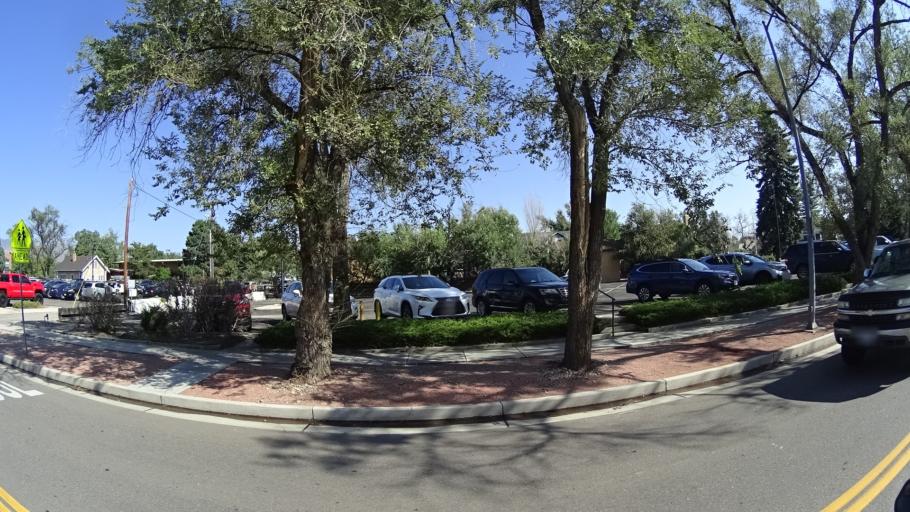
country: US
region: Colorado
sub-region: El Paso County
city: Colorado Springs
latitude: 38.8669
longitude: -104.8225
